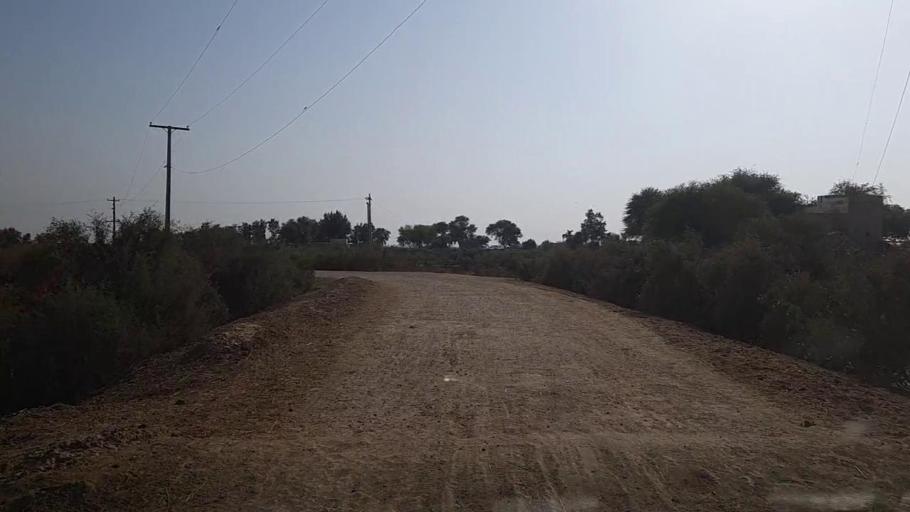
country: PK
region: Sindh
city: Kandhkot
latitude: 28.3815
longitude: 69.3354
